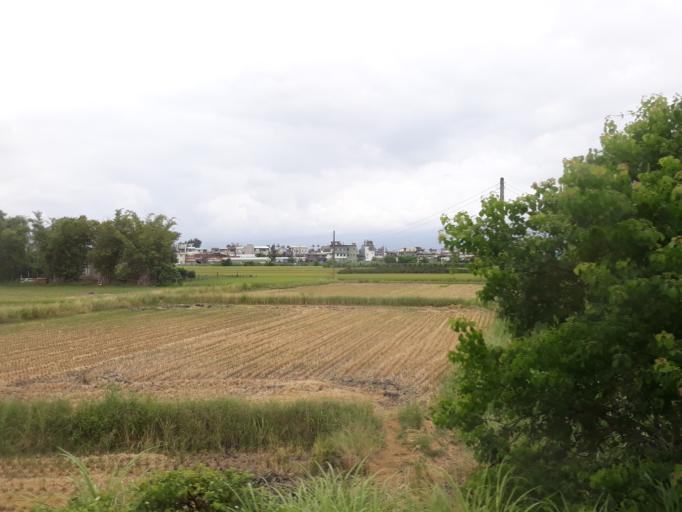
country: TW
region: Taiwan
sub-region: Yilan
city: Yilan
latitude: 24.6889
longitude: 121.7749
